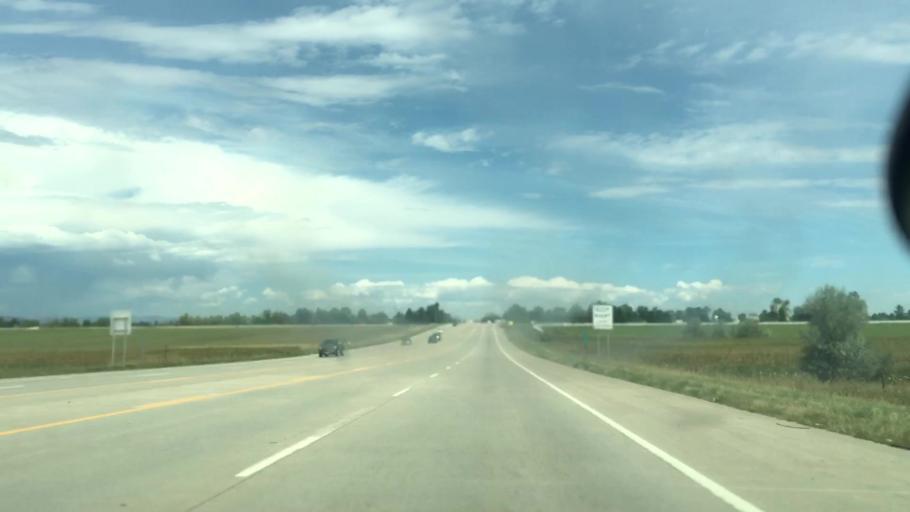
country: US
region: Colorado
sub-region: Boulder County
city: Longmont
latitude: 40.2271
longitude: -105.1023
